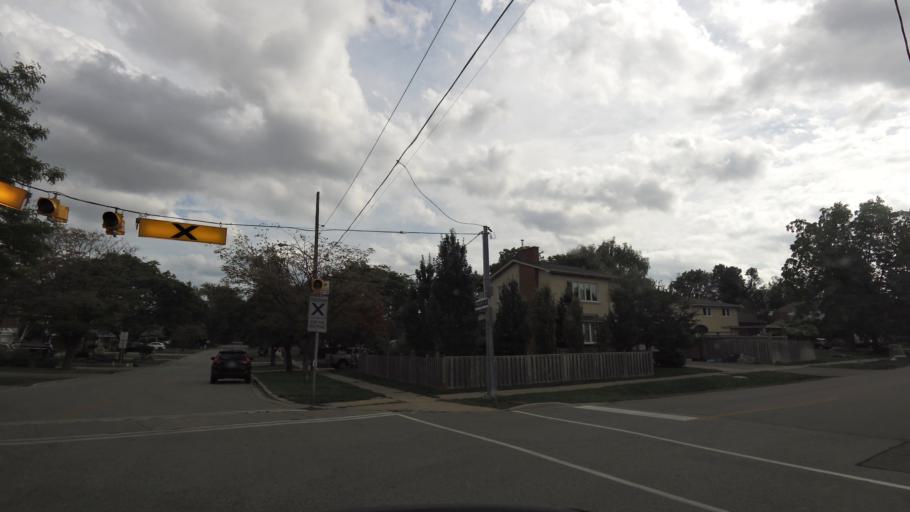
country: CA
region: Ontario
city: Etobicoke
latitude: 43.6448
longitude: -79.5841
